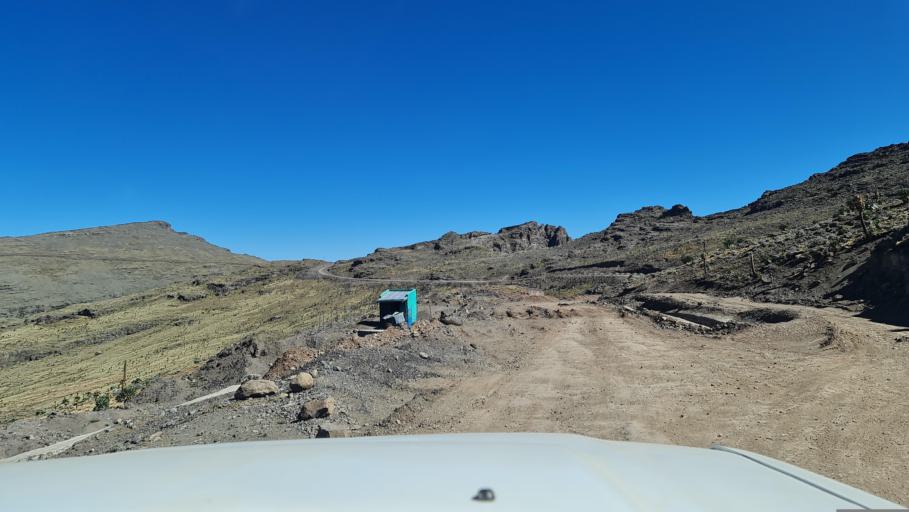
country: ET
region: Amhara
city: Debark'
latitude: 13.2136
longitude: 38.2175
